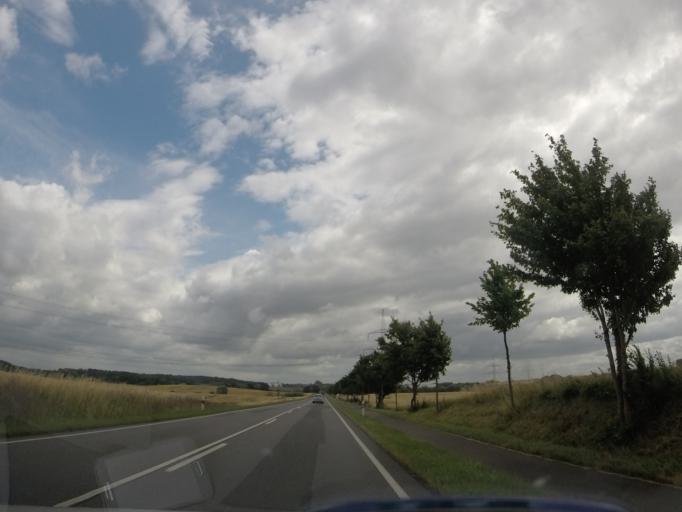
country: DE
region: Mecklenburg-Vorpommern
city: Lalendorf
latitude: 53.7627
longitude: 12.3604
